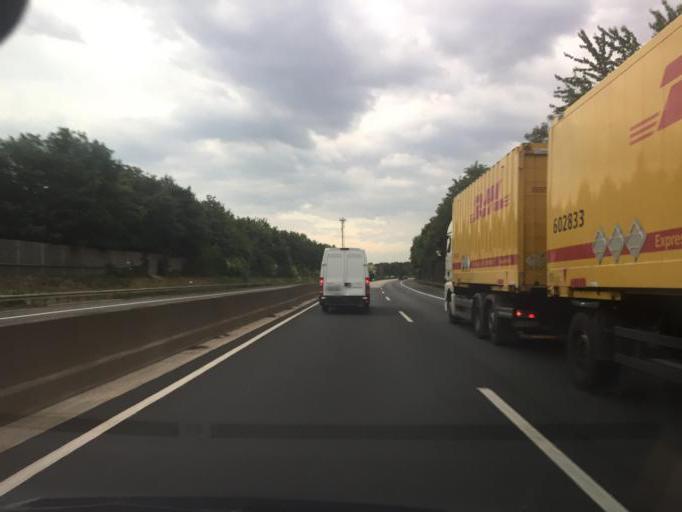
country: DE
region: North Rhine-Westphalia
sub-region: Regierungsbezirk Koln
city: Bedburg
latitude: 50.9918
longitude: 6.5513
